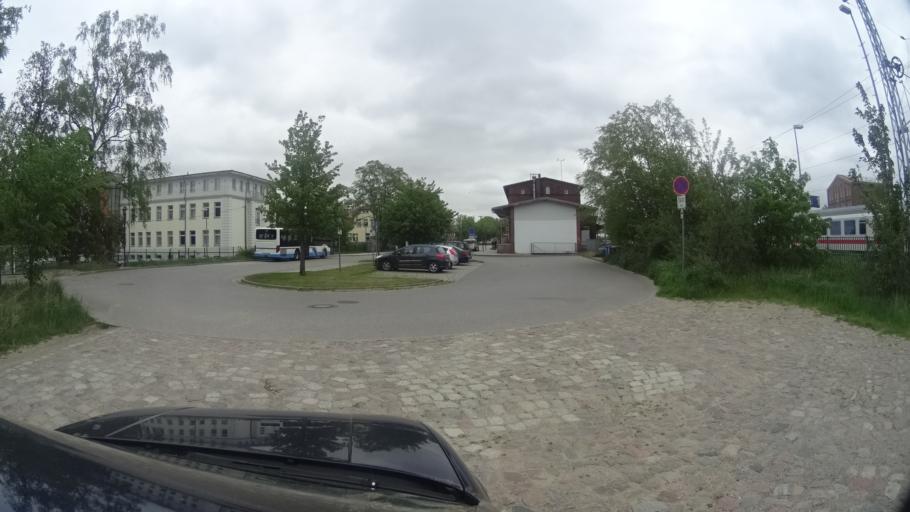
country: DE
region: Mecklenburg-Vorpommern
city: Ribnitz-Damgarten
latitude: 54.2393
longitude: 12.4356
